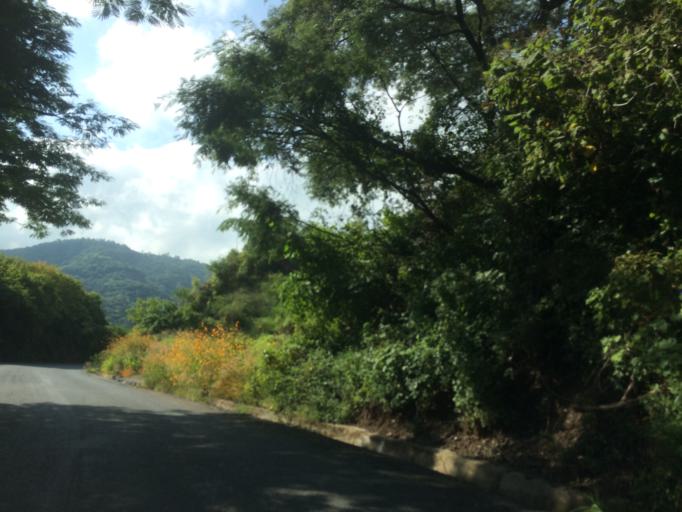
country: MX
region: Nayarit
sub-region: Ahuacatlan
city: Ahuacatlan
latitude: 21.0102
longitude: -104.4780
